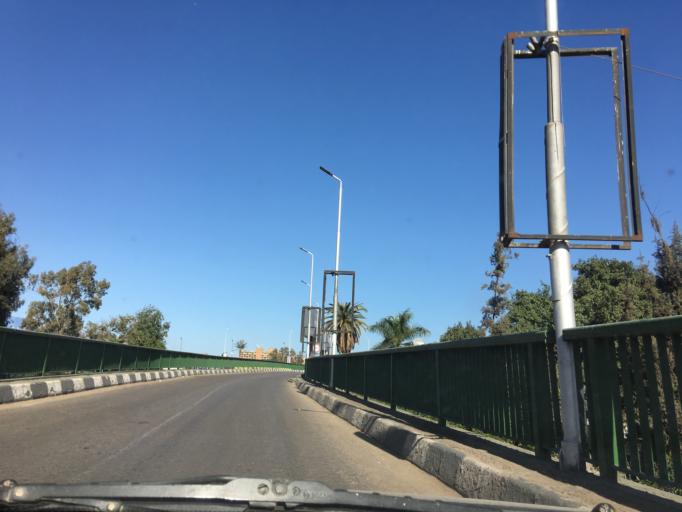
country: EG
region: Muhafazat al Qahirah
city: Cairo
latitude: 30.0477
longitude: 31.2268
